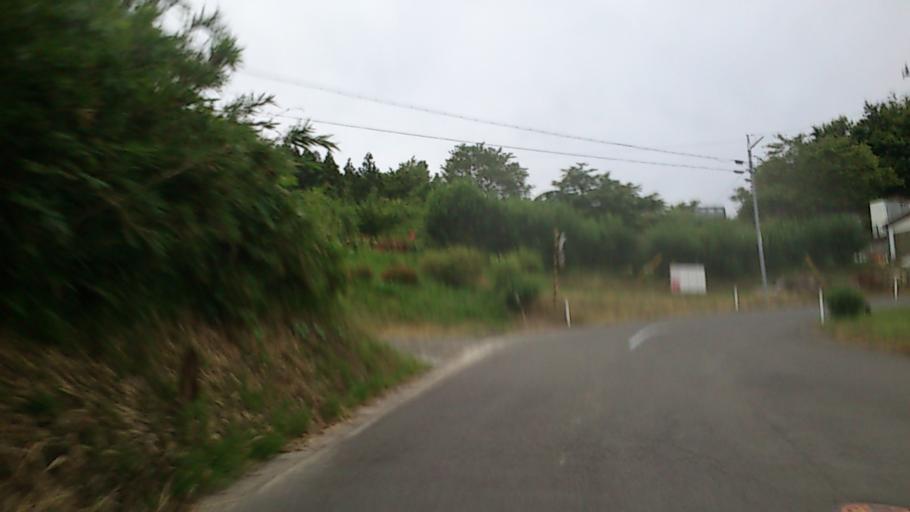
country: JP
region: Fukushima
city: Fukushima-shi
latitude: 37.6684
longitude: 140.5082
